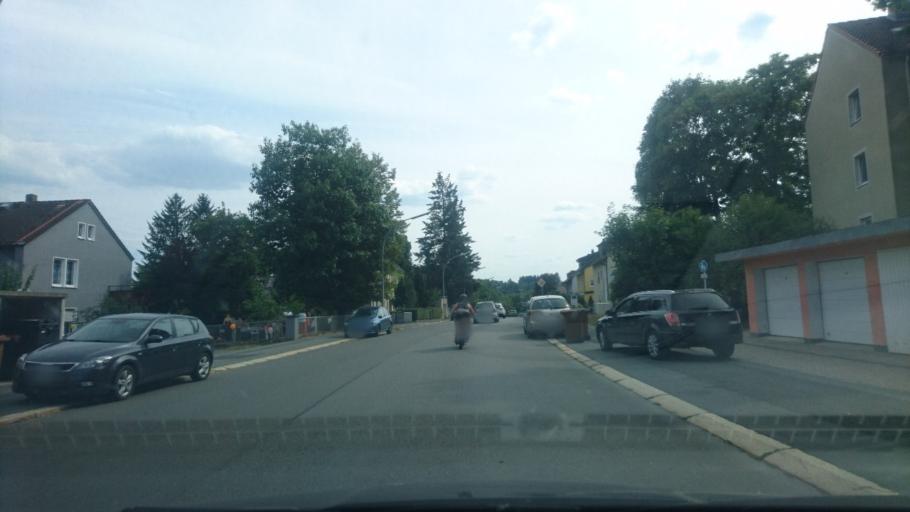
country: DE
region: Bavaria
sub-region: Upper Franconia
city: Hof
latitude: 50.3163
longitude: 11.9015
